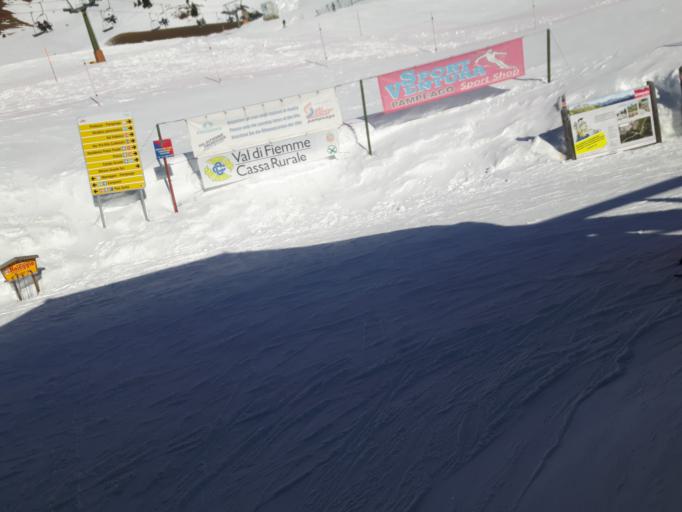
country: IT
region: Trentino-Alto Adige
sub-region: Provincia di Trento
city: Panchia
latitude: 46.3506
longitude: 11.5475
